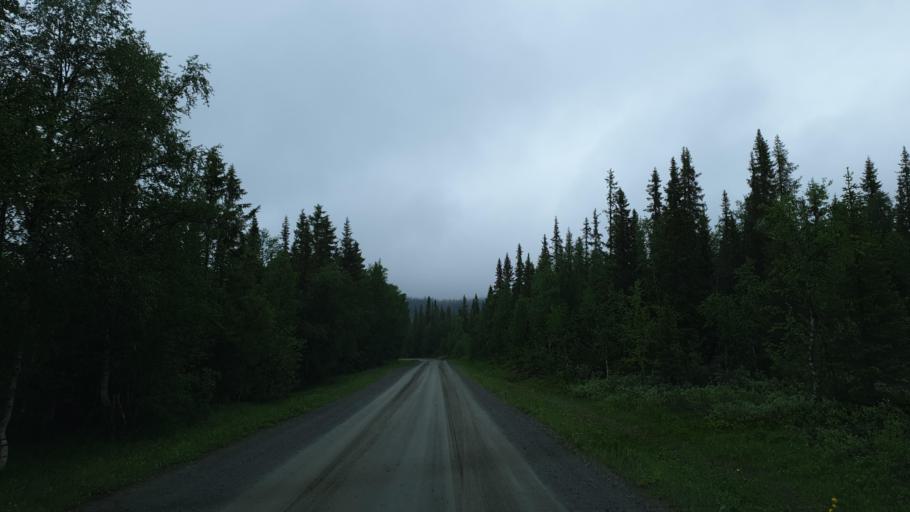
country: SE
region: Vaesterbotten
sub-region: Vilhelmina Kommun
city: Sjoberg
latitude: 65.3375
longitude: 15.8738
